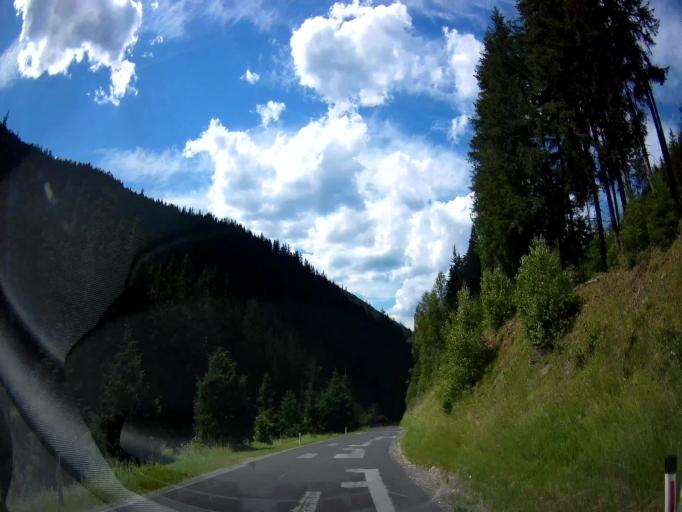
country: AT
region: Styria
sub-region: Politischer Bezirk Murau
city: Stadl an der Mur
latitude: 47.0313
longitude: 14.0070
